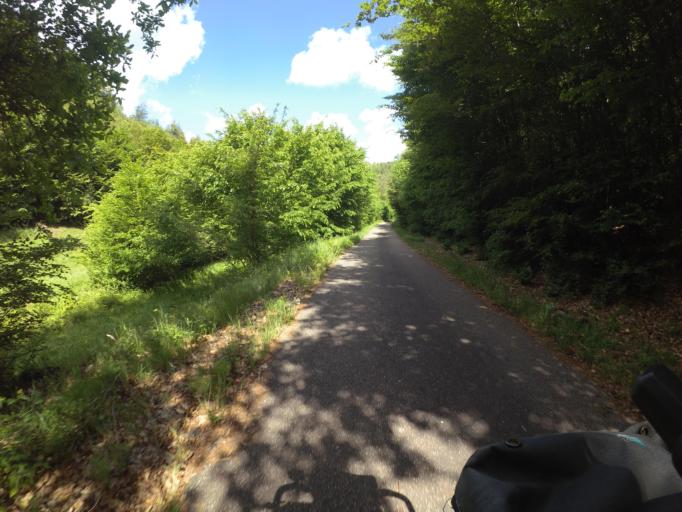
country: DE
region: Rheinland-Pfalz
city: Fischbach
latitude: 49.1150
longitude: 7.6921
